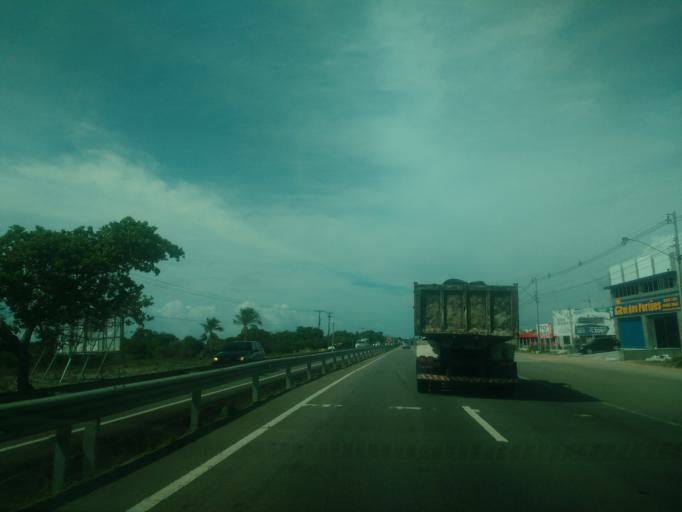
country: BR
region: Alagoas
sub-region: Marechal Deodoro
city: Marechal Deodoro
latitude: -9.7431
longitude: -35.8369
